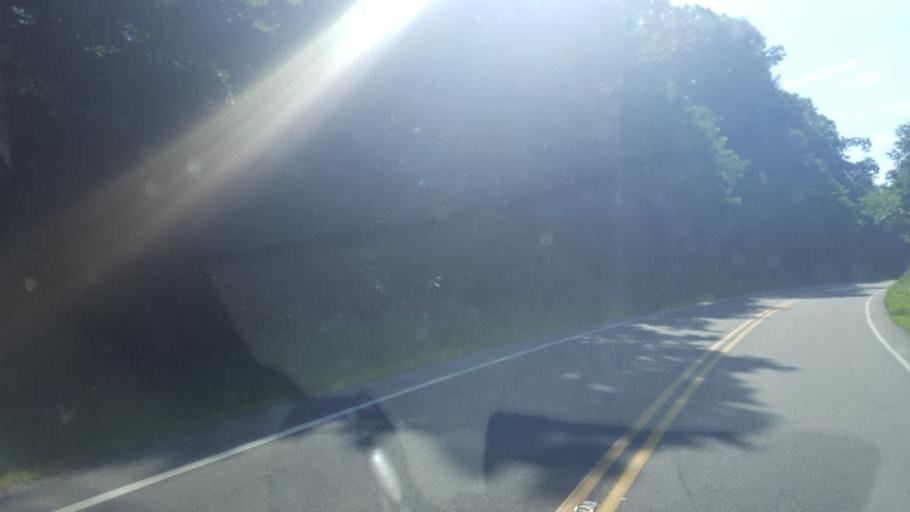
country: US
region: North Carolina
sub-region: Avery County
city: Newland
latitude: 36.0350
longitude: -81.9100
